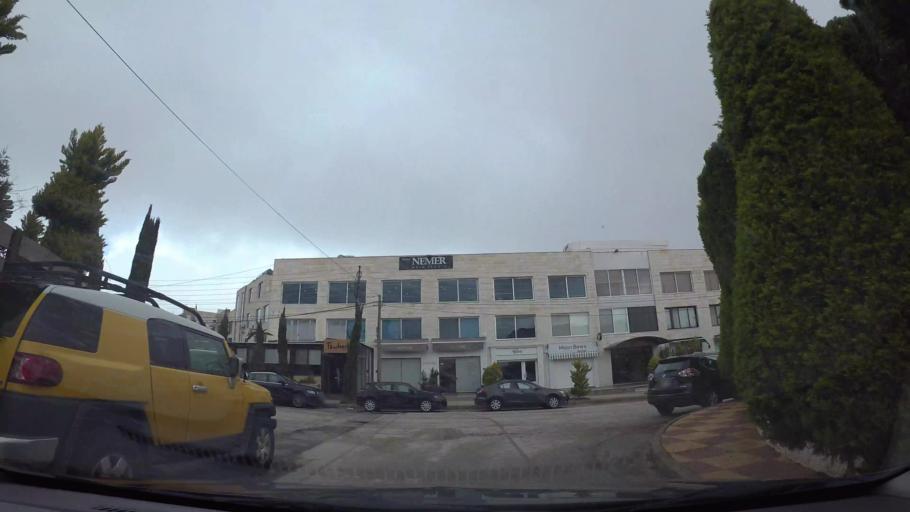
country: JO
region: Amman
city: Al Bunayyat ash Shamaliyah
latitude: 31.9461
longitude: 35.8774
